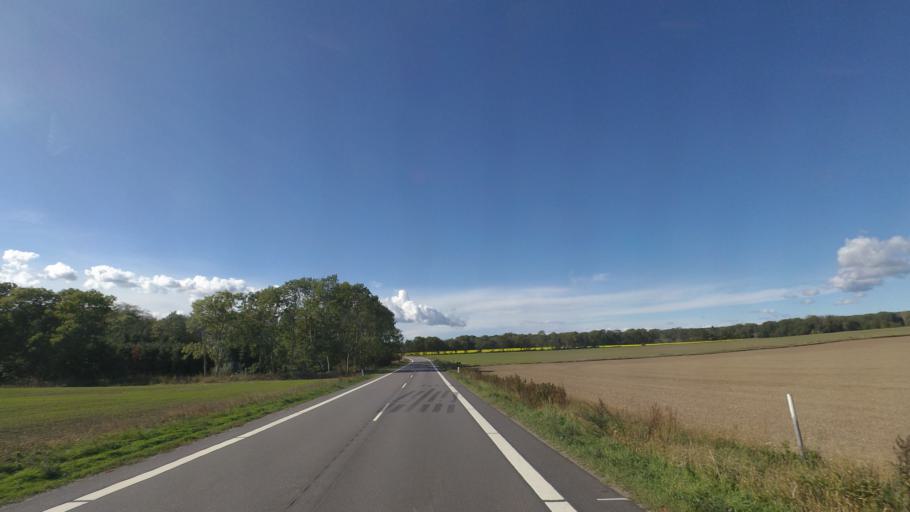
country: DK
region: Capital Region
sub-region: Bornholm Kommune
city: Akirkeby
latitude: 55.0688
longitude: 14.9857
